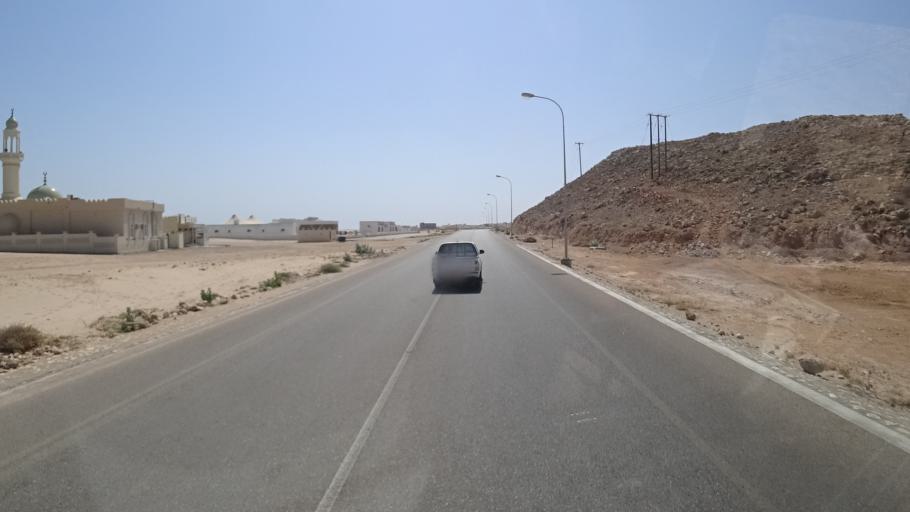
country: OM
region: Ash Sharqiyah
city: Sur
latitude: 22.5655
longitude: 59.5740
